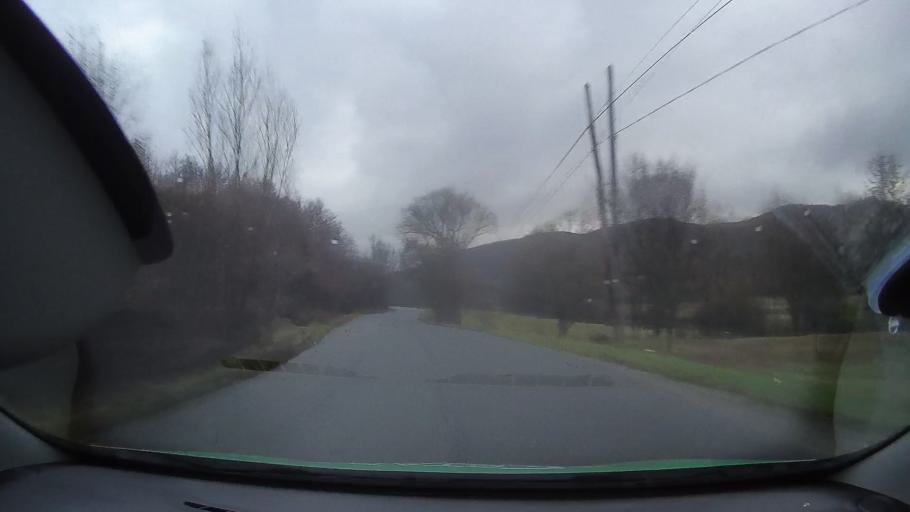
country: RO
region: Hunedoara
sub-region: Comuna Baia de Cris
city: Baia de Cris
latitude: 46.2041
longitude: 22.7170
